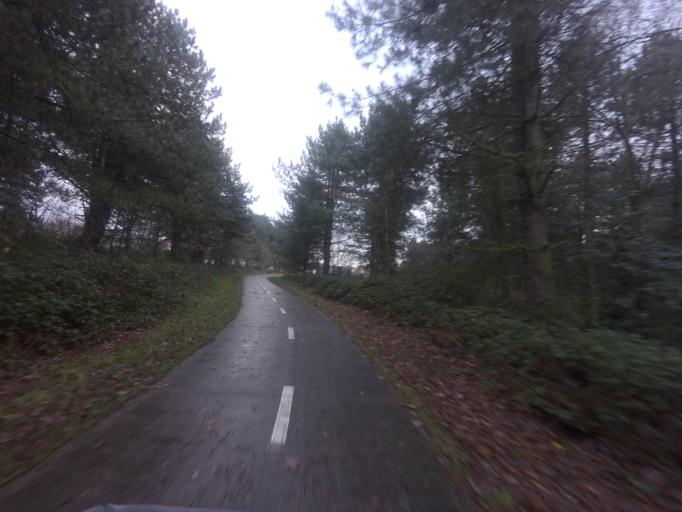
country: NL
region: North Holland
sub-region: Gemeente Texel
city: Den Burg
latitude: 53.1554
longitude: 4.8622
